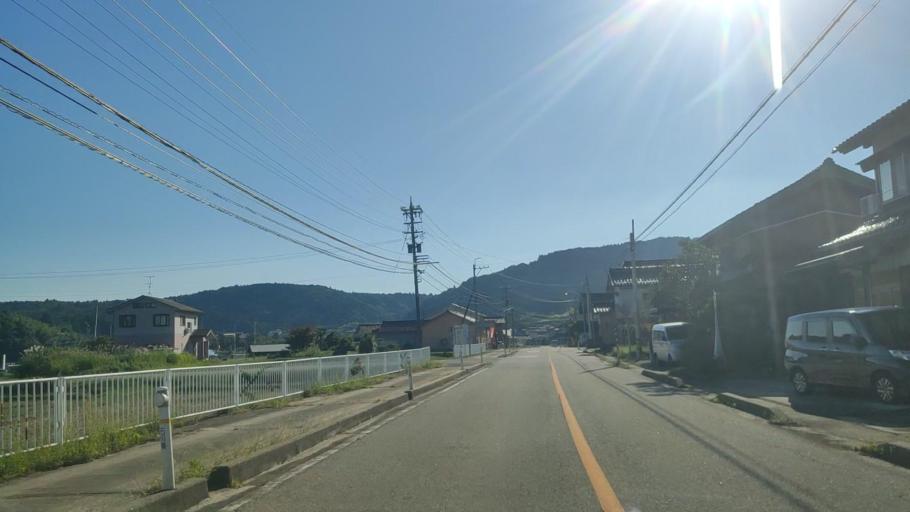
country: JP
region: Ishikawa
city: Nanao
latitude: 37.1481
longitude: 136.8757
